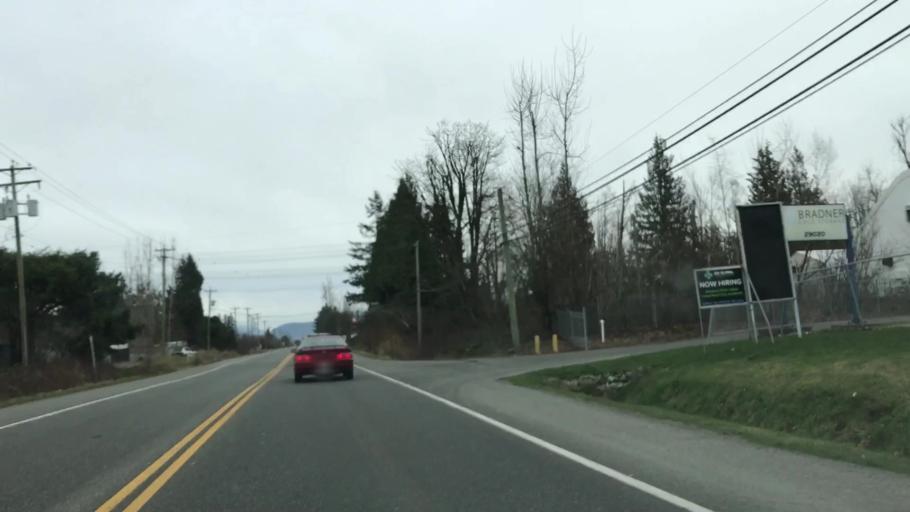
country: CA
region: British Columbia
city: Aldergrove
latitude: 49.0572
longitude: -122.4199
